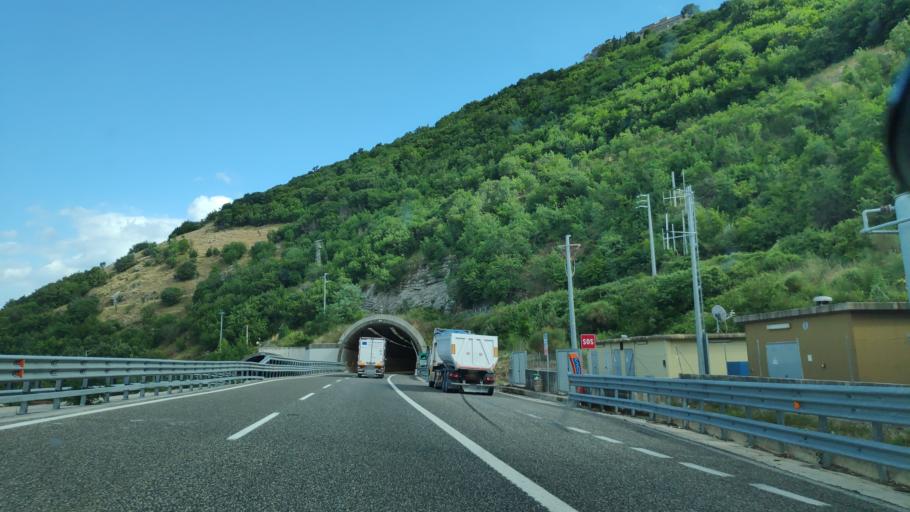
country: IT
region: Campania
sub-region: Provincia di Salerno
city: Sicignano degli Alburni
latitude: 40.5839
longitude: 15.3410
